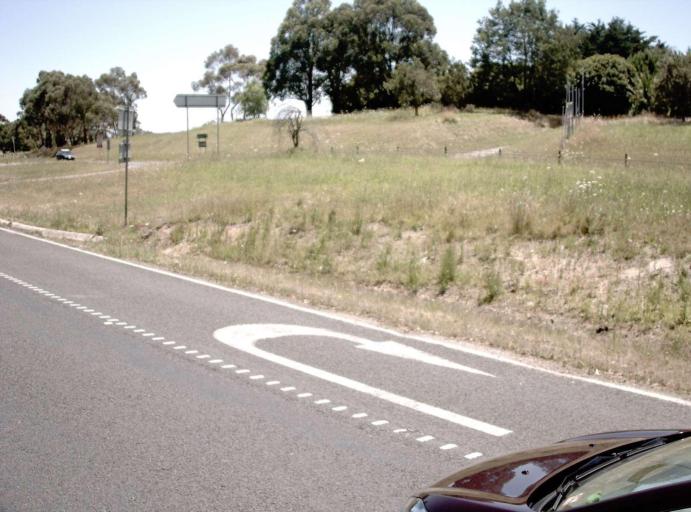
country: AU
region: Victoria
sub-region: Cardinia
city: Garfield
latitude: -38.0763
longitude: 145.6754
